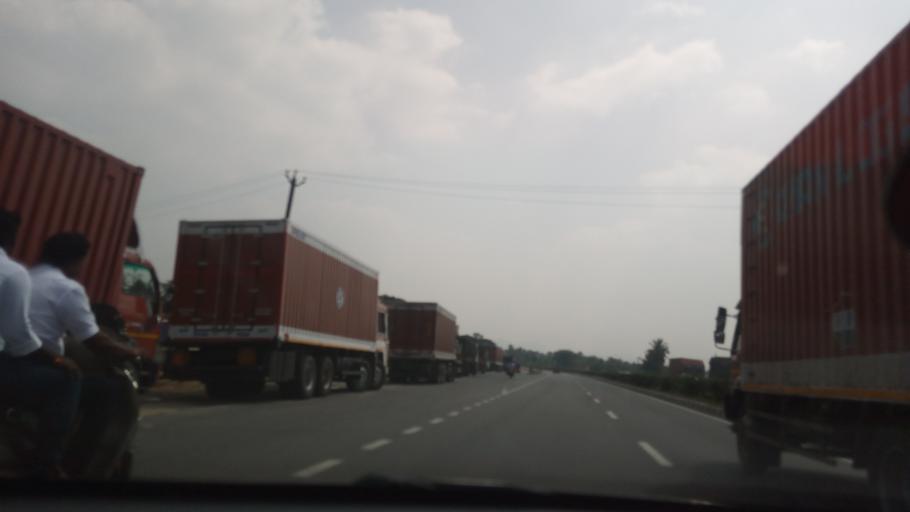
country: IN
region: Tamil Nadu
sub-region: Krishnagiri
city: Kaverippattanam
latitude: 12.4578
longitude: 78.2155
